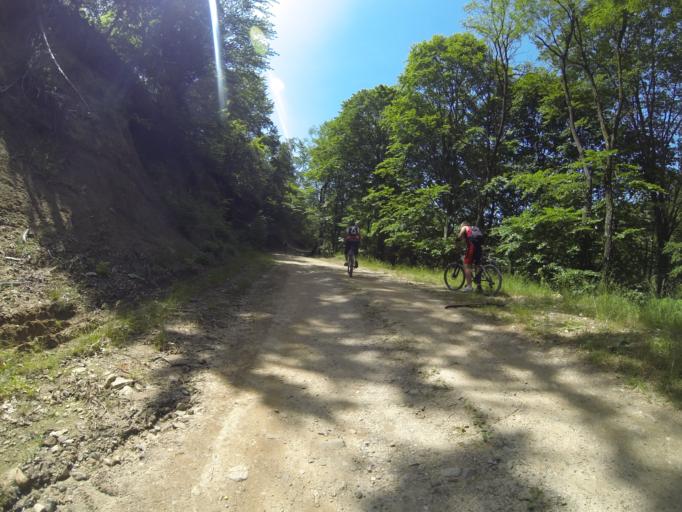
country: RO
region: Valcea
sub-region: Oras Baile Olanesti
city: Baile Olanesti
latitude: 45.2090
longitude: 24.2161
